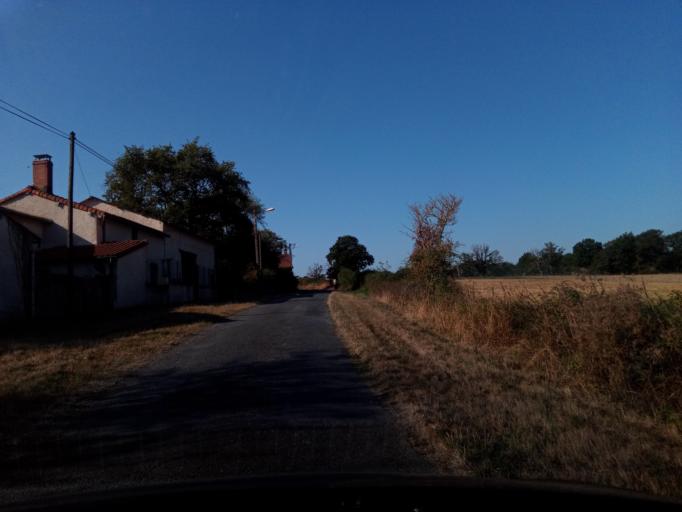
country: FR
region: Poitou-Charentes
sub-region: Departement de la Vienne
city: Saulge
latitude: 46.3779
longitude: 0.8670
